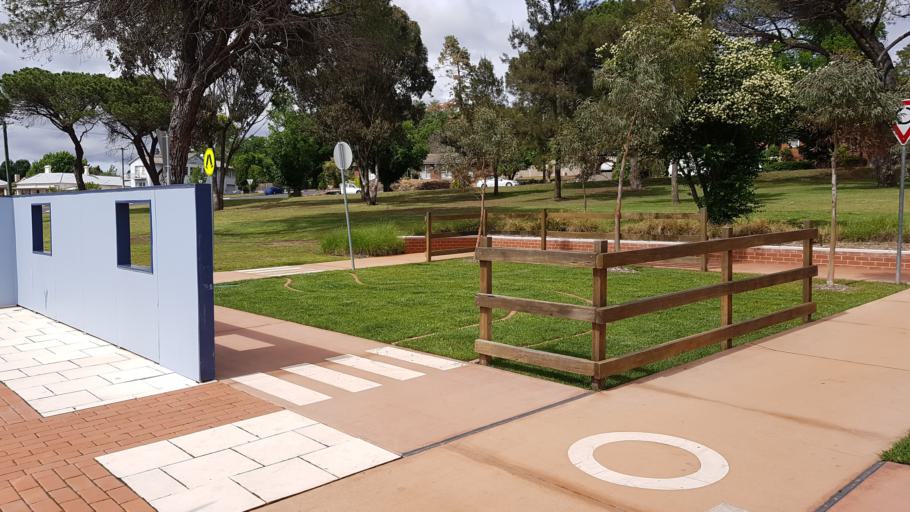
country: AU
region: New South Wales
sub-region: Bathurst Regional
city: Bathurst
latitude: -33.4084
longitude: 149.5737
